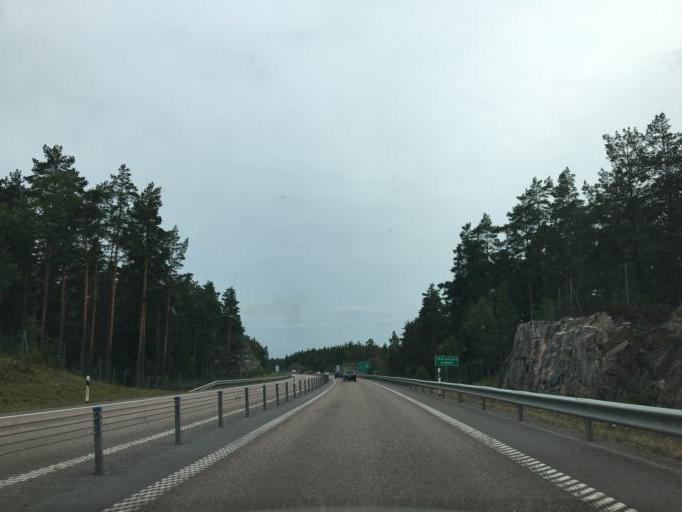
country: SE
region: Soedermanland
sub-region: Strangnas Kommun
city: Strangnas
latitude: 59.3738
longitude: 16.9638
